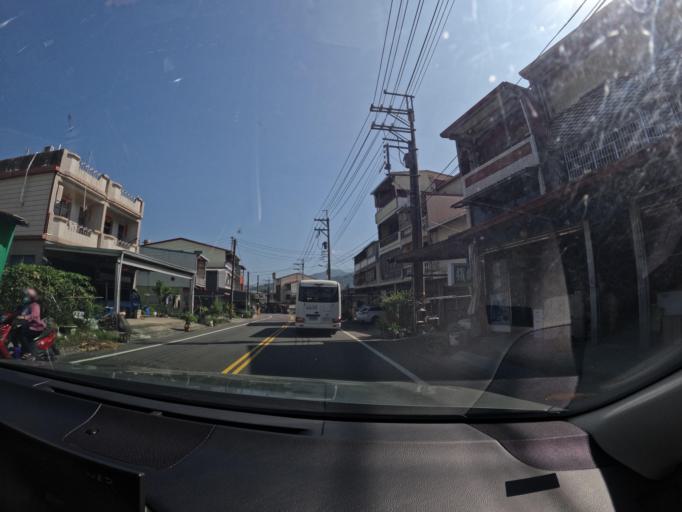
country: TW
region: Taiwan
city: Yujing
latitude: 23.0721
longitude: 120.6723
